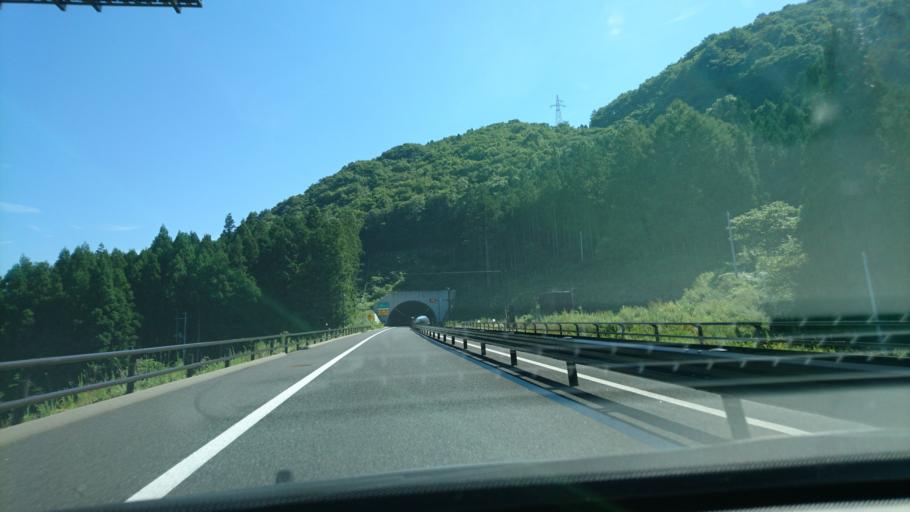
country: JP
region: Iwate
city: Tono
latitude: 39.3139
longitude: 141.4503
